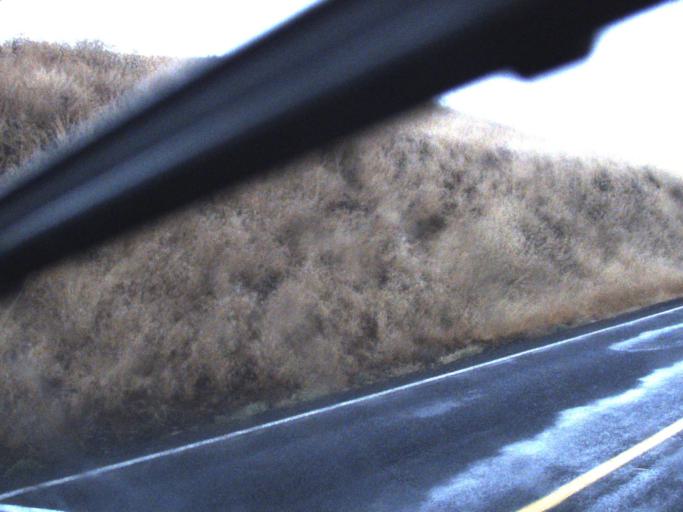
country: US
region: Washington
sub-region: Whitman County
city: Colfax
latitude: 47.0394
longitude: -117.5102
